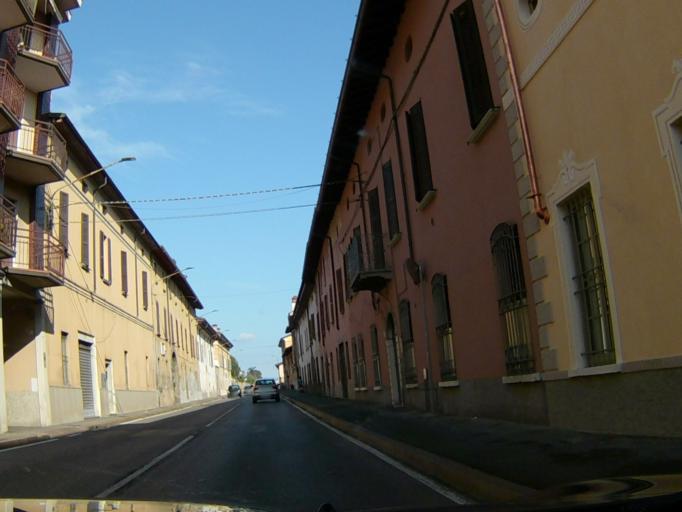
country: IT
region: Lombardy
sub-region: Provincia di Brescia
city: Coccaglio
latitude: 45.5627
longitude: 9.9802
